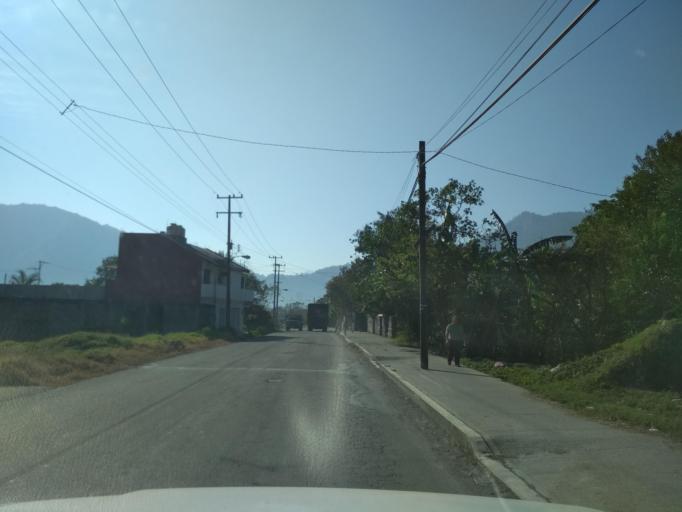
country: MX
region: Veracruz
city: Jalapilla
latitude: 18.8213
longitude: -97.0825
